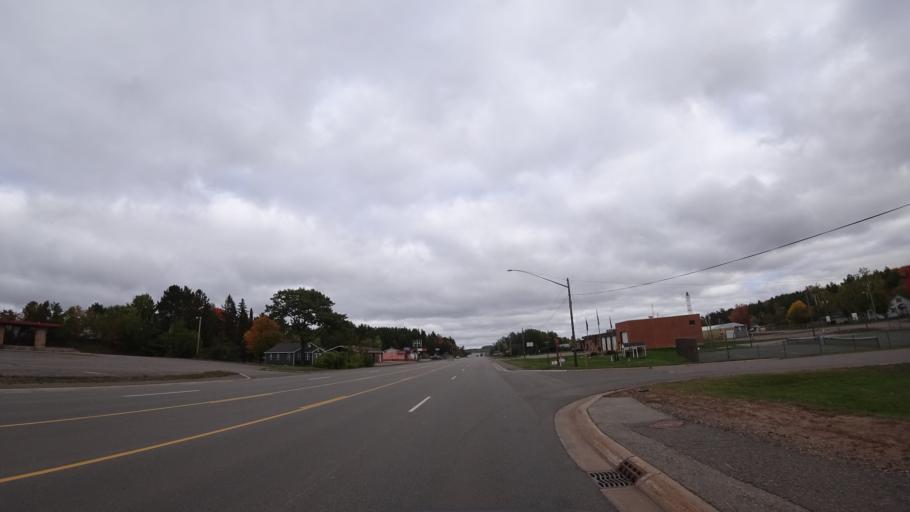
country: US
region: Michigan
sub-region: Marquette County
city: West Ishpeming
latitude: 46.4876
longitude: -87.7139
